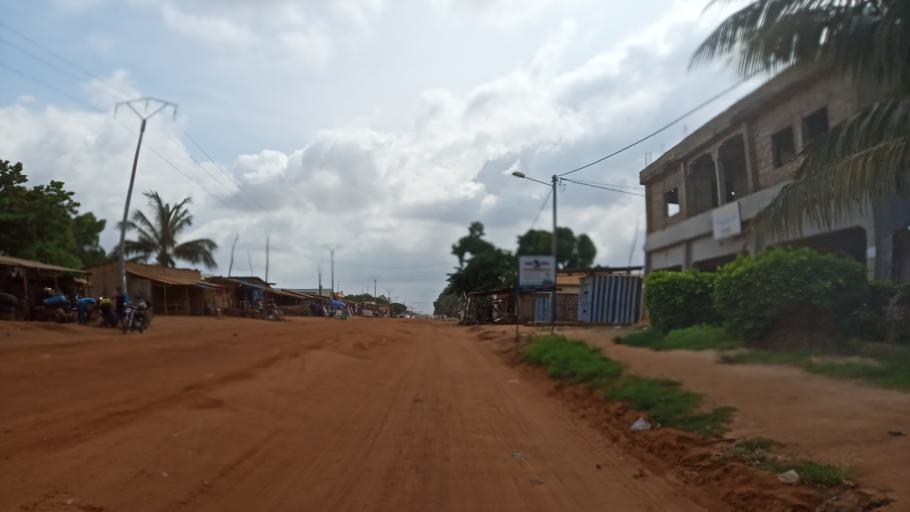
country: TG
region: Maritime
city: Lome
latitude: 6.2334
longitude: 1.1463
